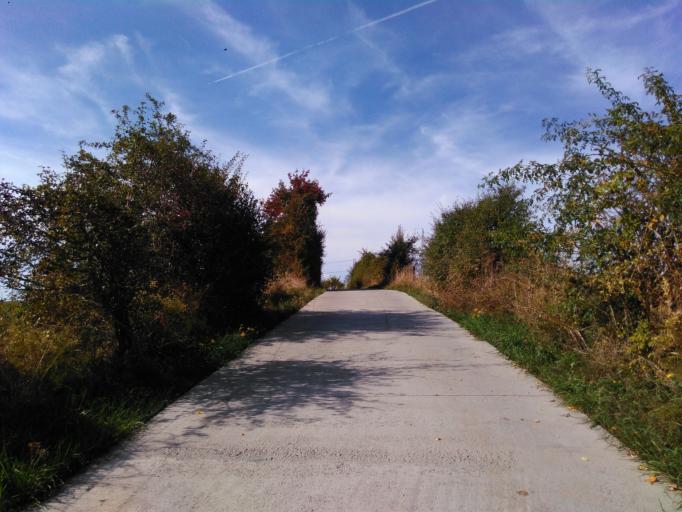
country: LU
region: Luxembourg
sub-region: Canton d'Esch-sur-Alzette
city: Sanem
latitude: 49.5507
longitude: 5.9167
